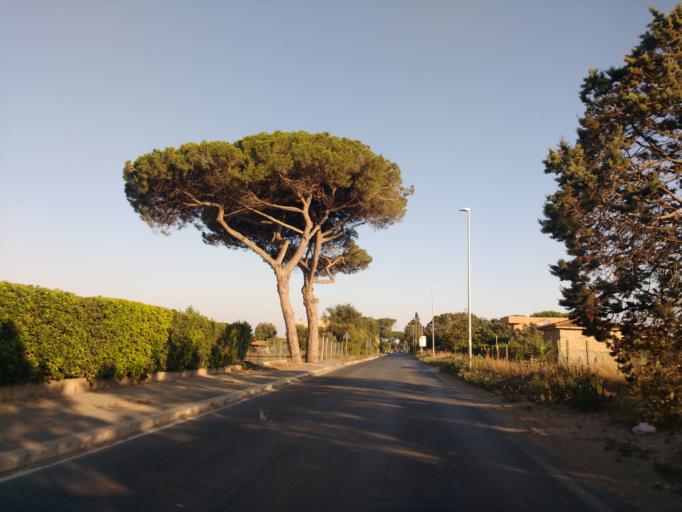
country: IT
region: Latium
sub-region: Citta metropolitana di Roma Capitale
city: Focene
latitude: 41.8399
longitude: 12.2266
